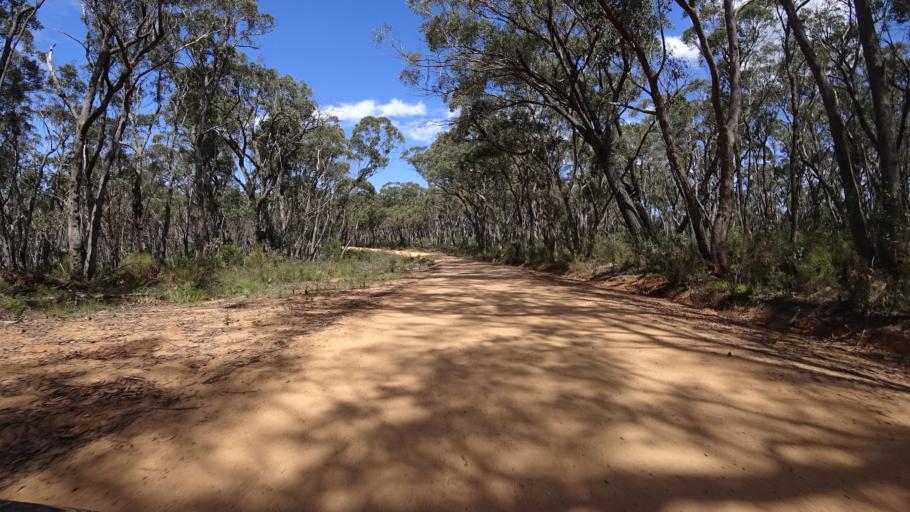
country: AU
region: New South Wales
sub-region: Lithgow
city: Lithgow
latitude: -33.3024
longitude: 150.2396
